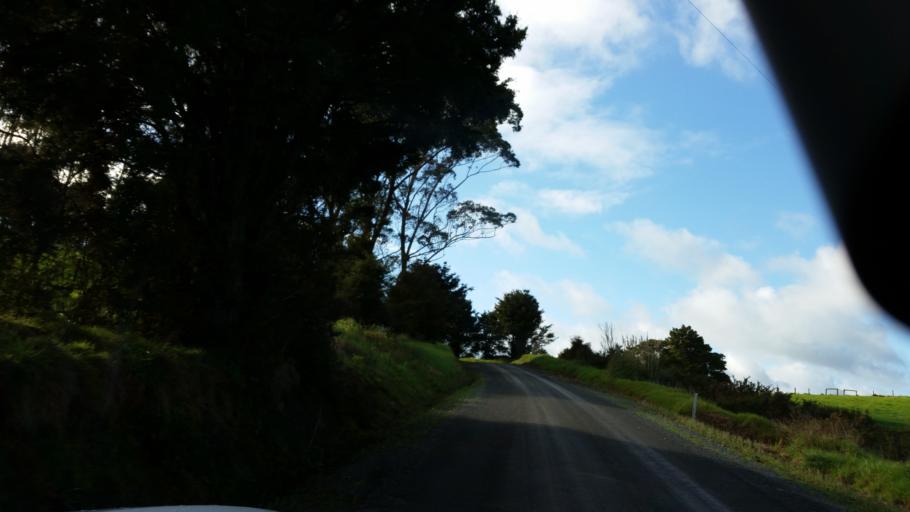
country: NZ
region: Northland
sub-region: Whangarei
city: Maungatapere
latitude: -35.6933
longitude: 174.1133
